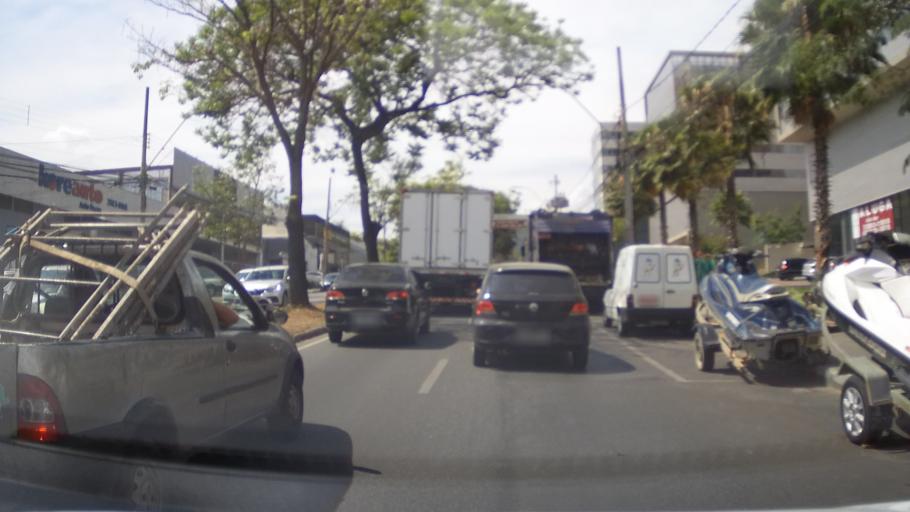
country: BR
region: Minas Gerais
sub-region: Belo Horizonte
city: Belo Horizonte
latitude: -19.9583
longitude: -43.9656
